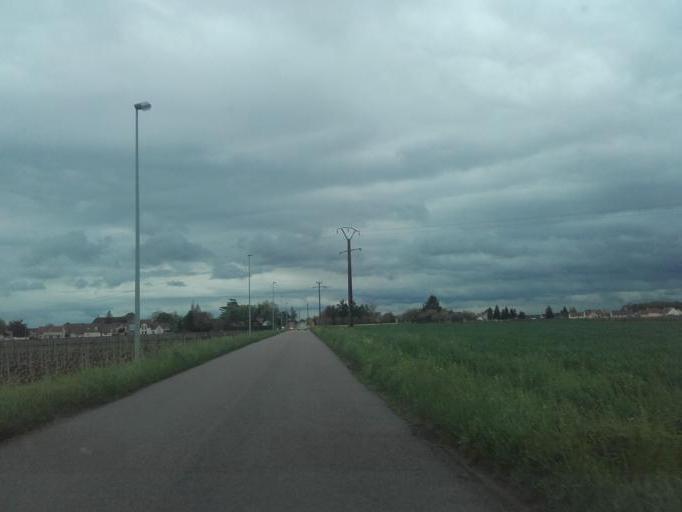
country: FR
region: Bourgogne
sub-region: Departement de la Cote-d'Or
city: Beaune
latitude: 47.0489
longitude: 4.8567
